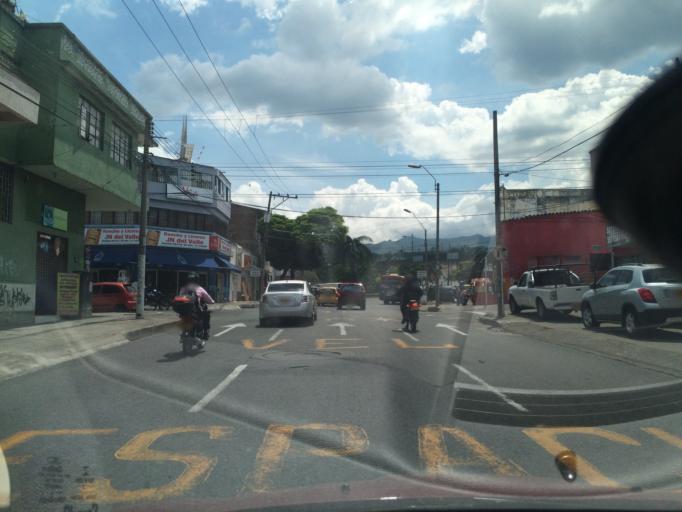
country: CO
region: Valle del Cauca
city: Cali
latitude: 3.4380
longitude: -76.5370
